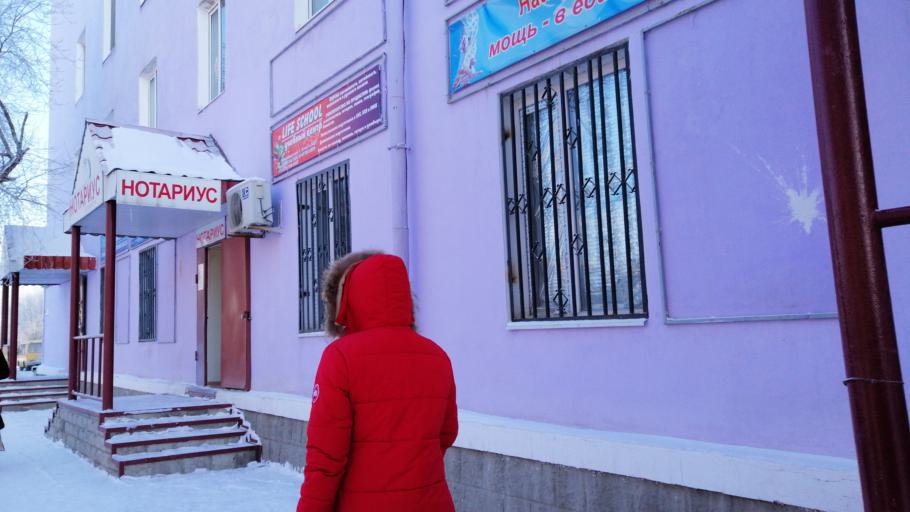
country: KZ
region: Aqtoebe
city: Aqtobe
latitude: 50.3109
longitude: 57.1470
